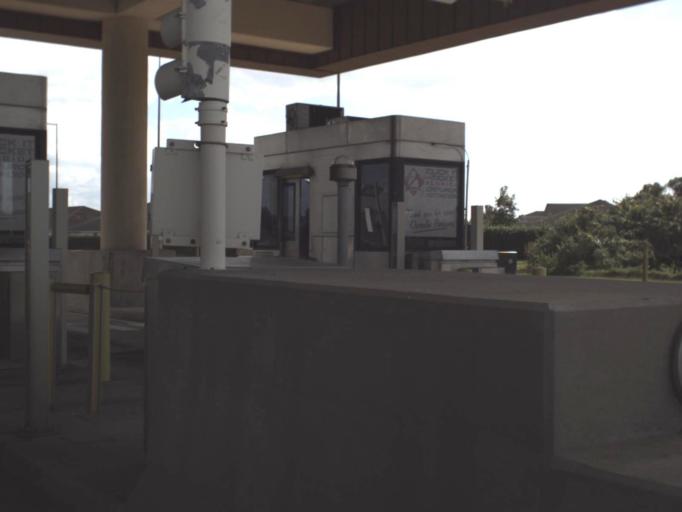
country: US
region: Florida
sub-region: Orange County
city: Hunters Creek
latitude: 28.3453
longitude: -81.4402
